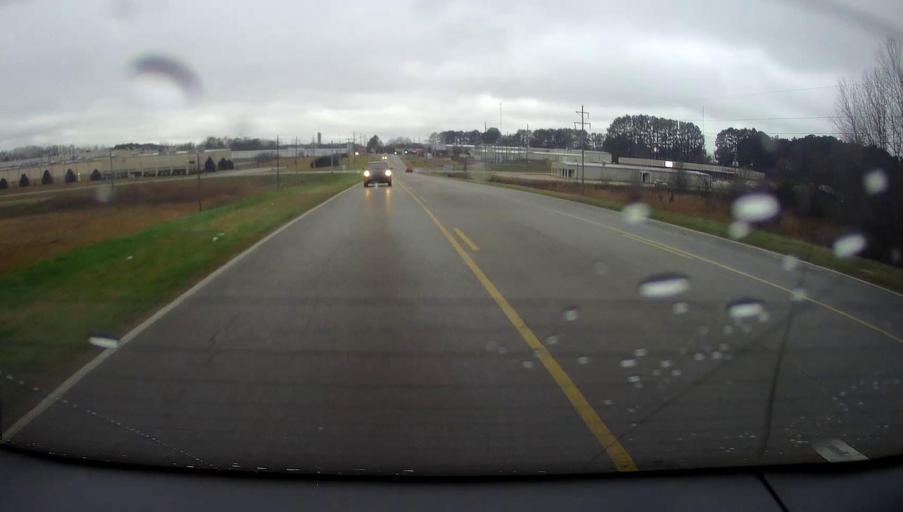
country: US
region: Mississippi
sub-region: Alcorn County
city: Corinth
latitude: 34.9090
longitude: -88.5150
